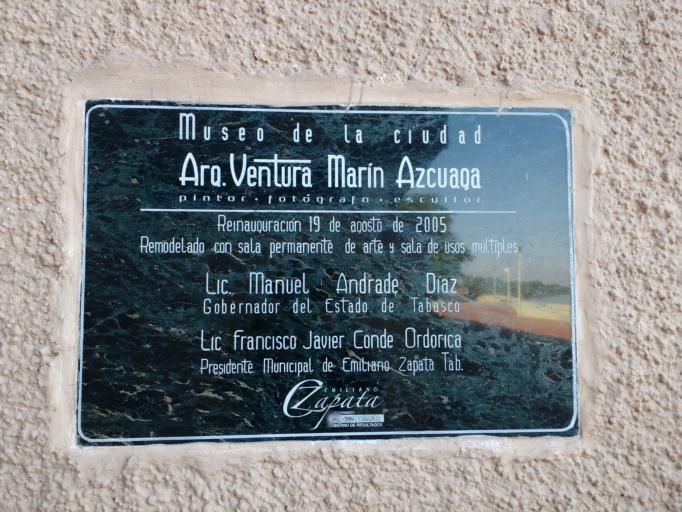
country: MX
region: Chiapas
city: Emiliano Zapata
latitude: 17.7453
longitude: -91.7651
